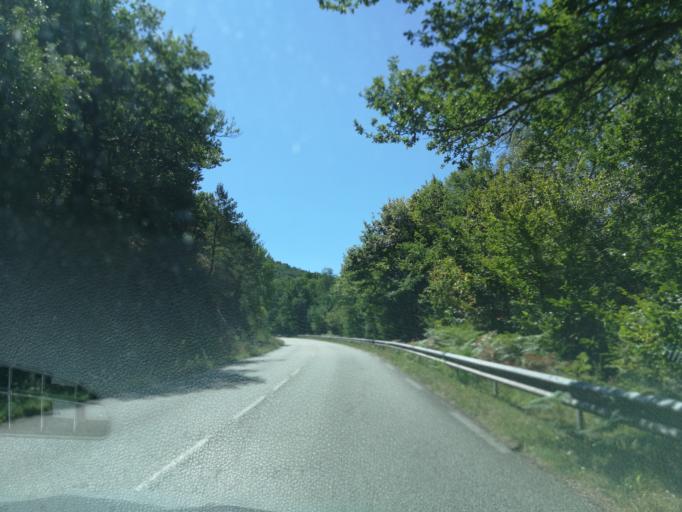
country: FR
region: Limousin
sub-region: Departement de la Correze
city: Argentat
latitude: 45.0693
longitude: 1.9457
